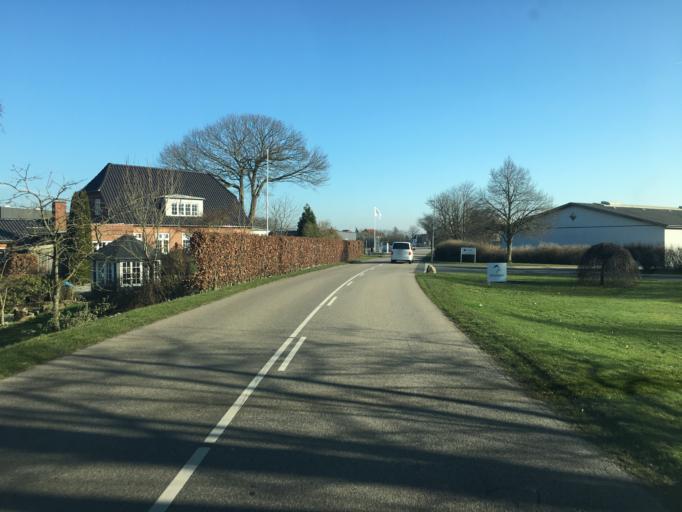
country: DK
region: South Denmark
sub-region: Sonderborg Kommune
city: Dybbol
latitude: 54.9287
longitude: 9.7292
